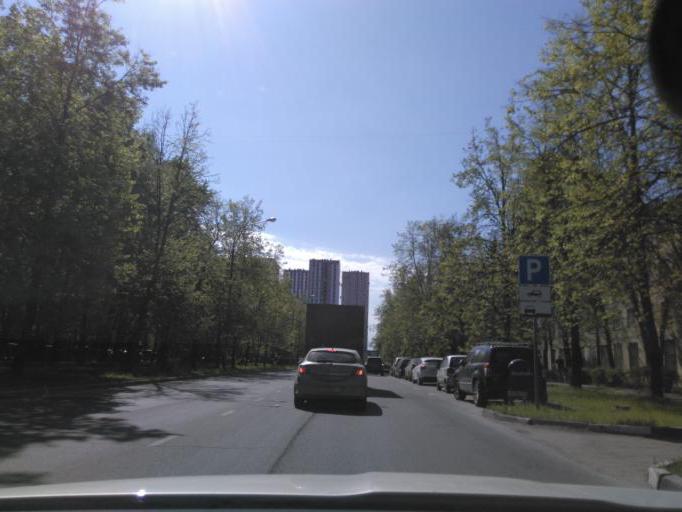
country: RU
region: Moskovskaya
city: Levoberezhnyy
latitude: 55.8451
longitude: 37.4901
